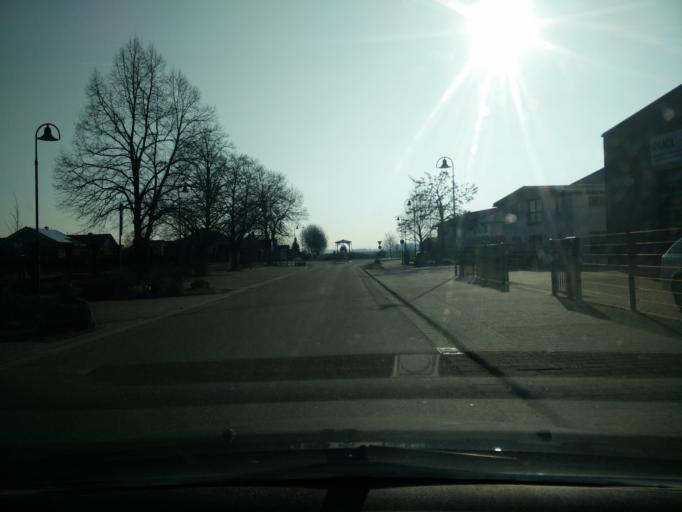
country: DE
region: Rheinland-Pfalz
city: Steinweiler
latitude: 49.1186
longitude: 8.1426
